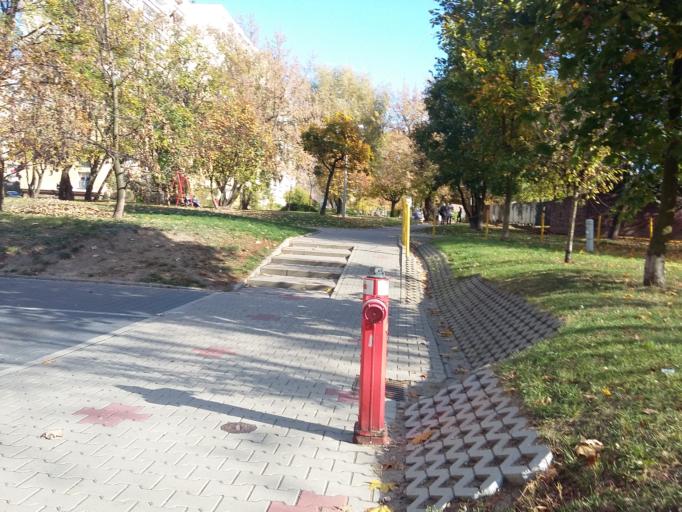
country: PL
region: Lodz Voivodeship
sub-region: Powiat pabianicki
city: Ksawerow
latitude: 51.7456
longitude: 19.4026
